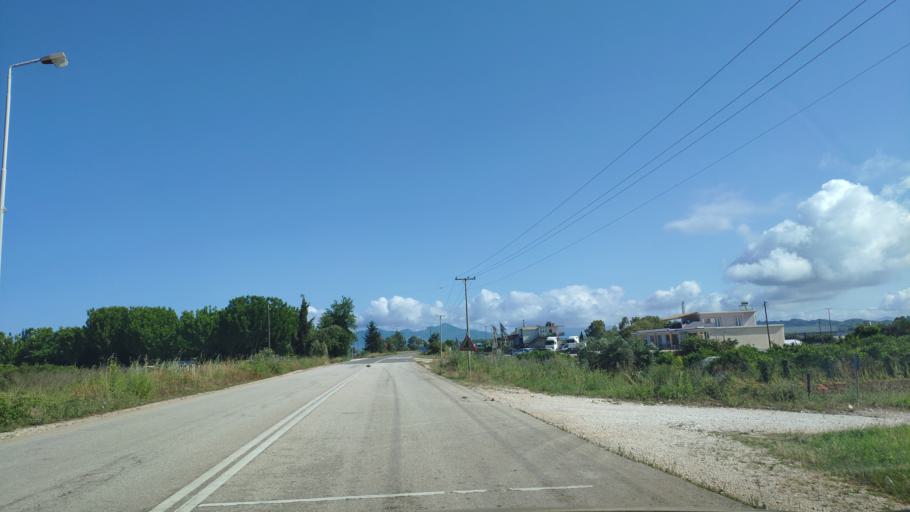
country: GR
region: Epirus
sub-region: Nomos Prevezis
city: Preveza
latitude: 38.9857
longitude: 20.7143
